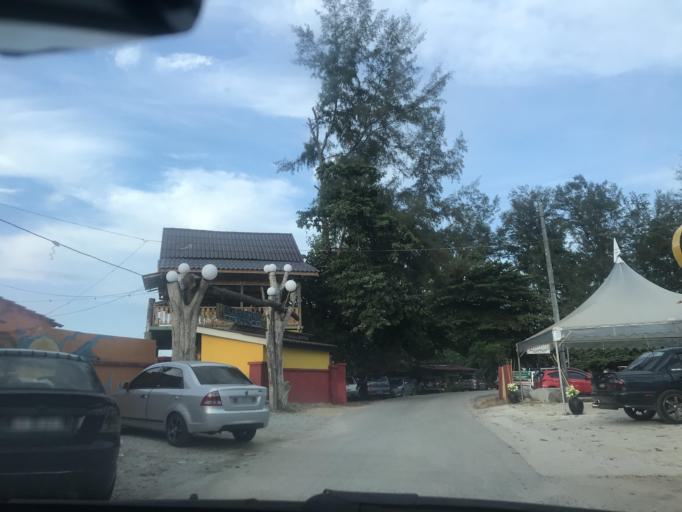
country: MY
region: Kelantan
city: Peringat
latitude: 6.1308
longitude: 102.3691
